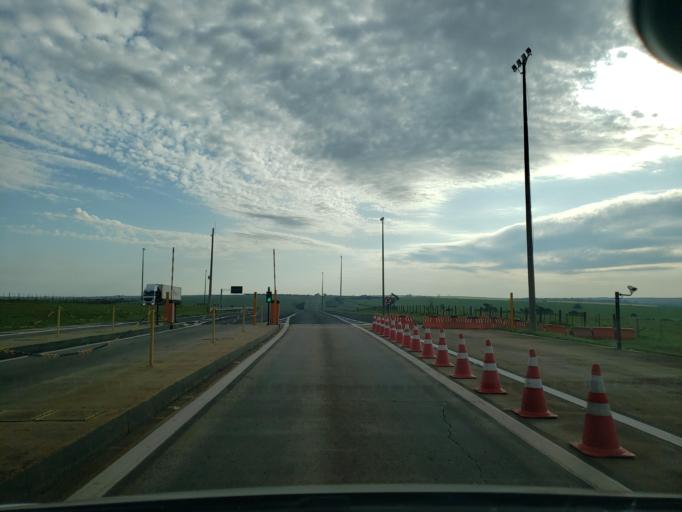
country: BR
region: Sao Paulo
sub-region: Guararapes
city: Guararapes
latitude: -21.2101
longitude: -50.7322
